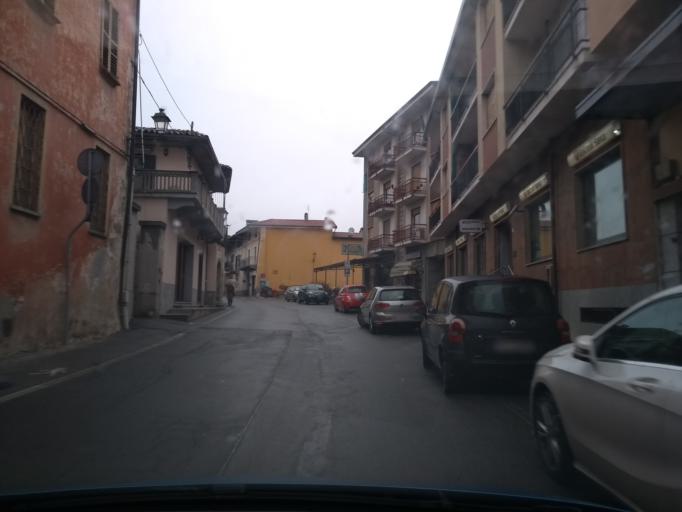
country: IT
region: Piedmont
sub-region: Provincia di Torino
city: Valperga
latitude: 45.3721
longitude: 7.6573
